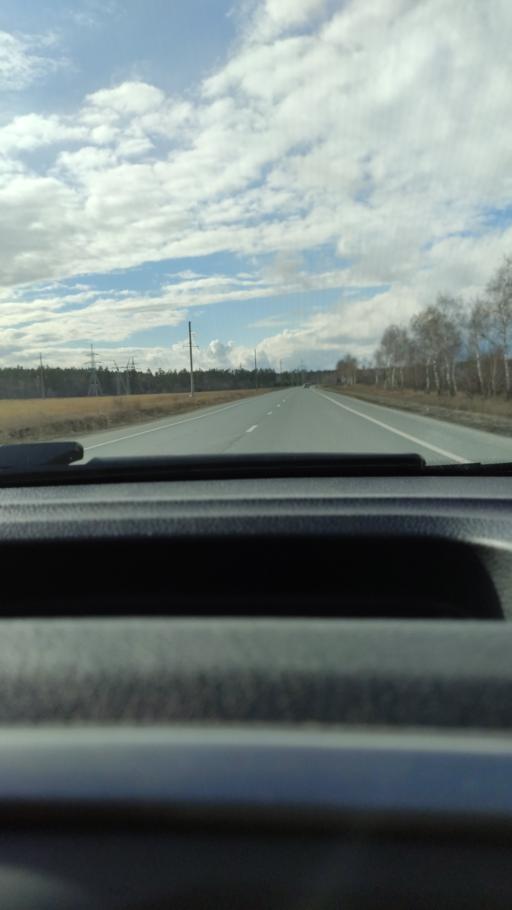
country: RU
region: Samara
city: Kurumoch
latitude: 53.4902
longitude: 49.9829
